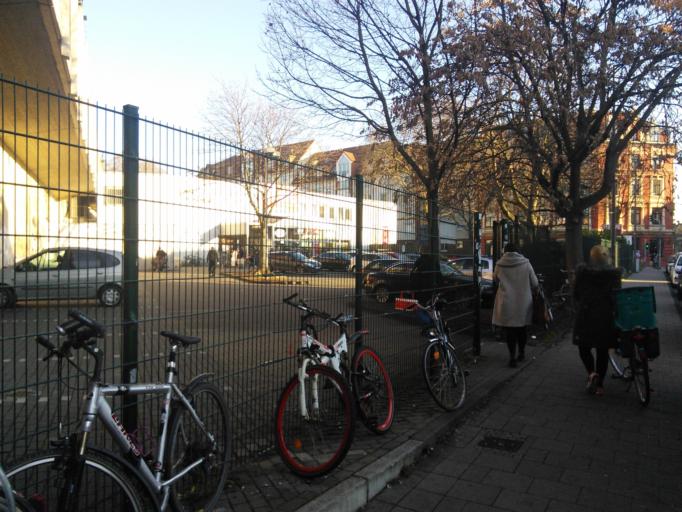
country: DE
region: North Rhine-Westphalia
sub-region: Regierungsbezirk Koln
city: Neuehrenfeld
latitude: 50.9521
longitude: 6.9248
